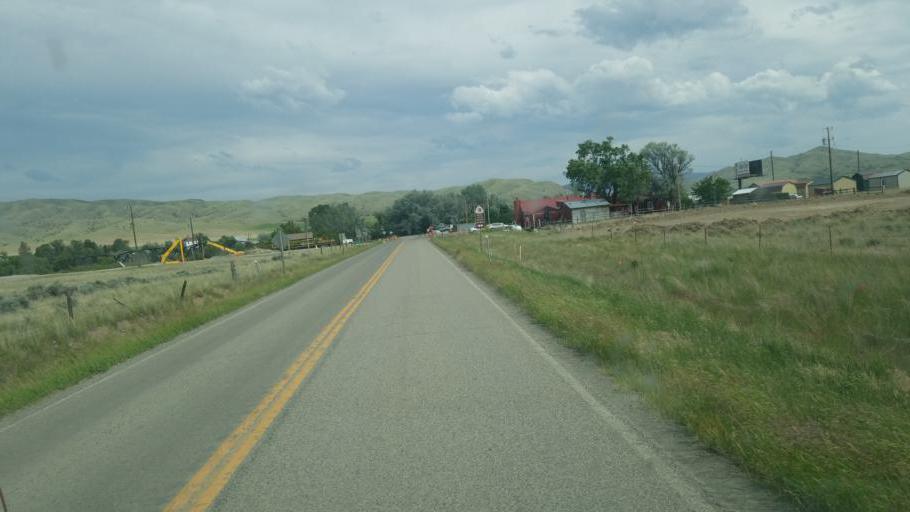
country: US
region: Montana
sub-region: Broadwater County
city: Townsend
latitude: 46.1727
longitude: -111.4489
